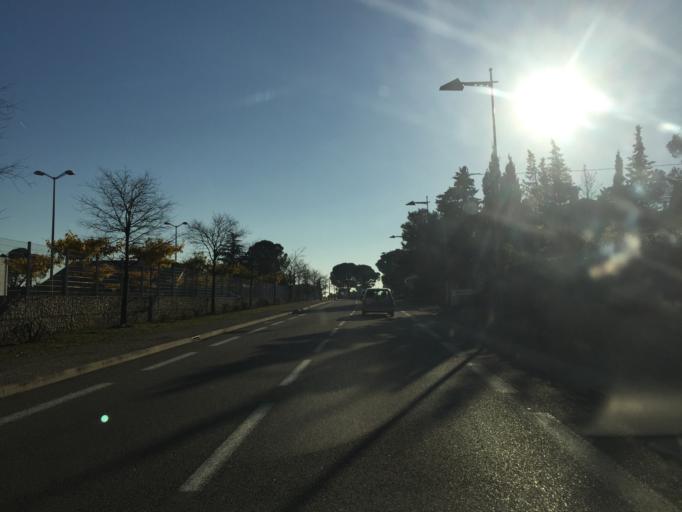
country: FR
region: Provence-Alpes-Cote d'Azur
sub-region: Departement du Vaucluse
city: Sainte-Cecile-les-Vignes
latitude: 44.2359
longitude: 4.8836
